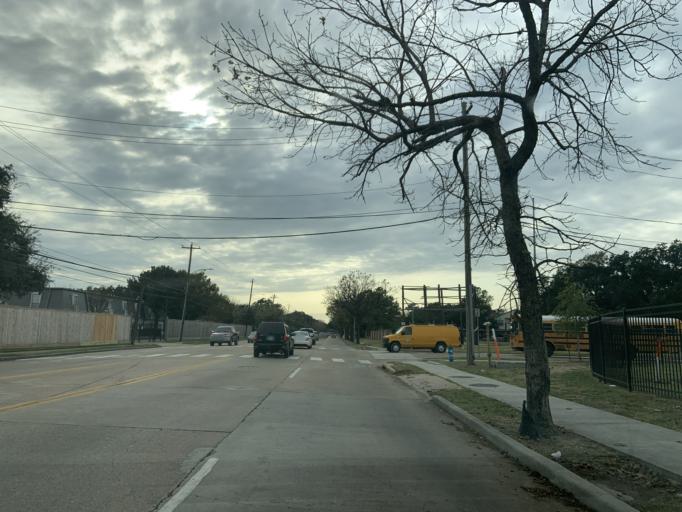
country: US
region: Texas
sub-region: Harris County
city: Bellaire
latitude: 29.6826
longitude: -95.5171
